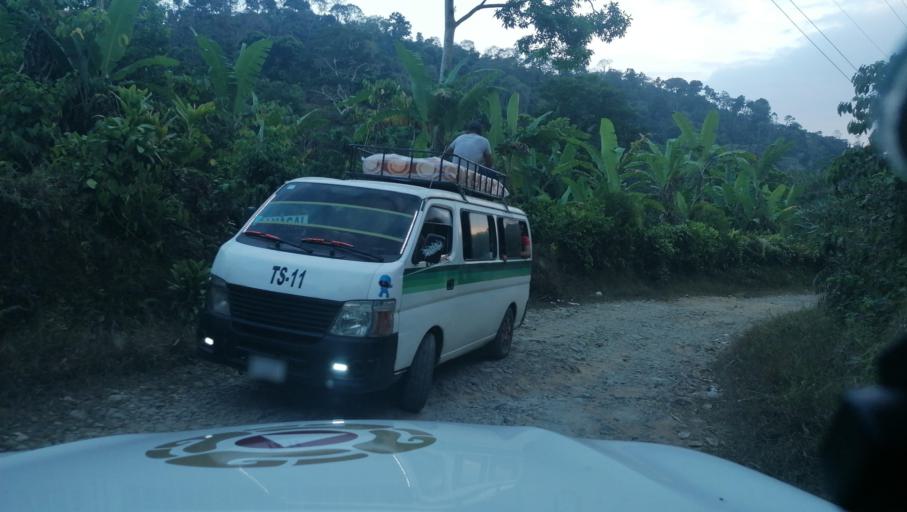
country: MX
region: Chiapas
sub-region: Cacahoatan
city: Benito Juarez
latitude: 15.0743
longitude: -92.2267
